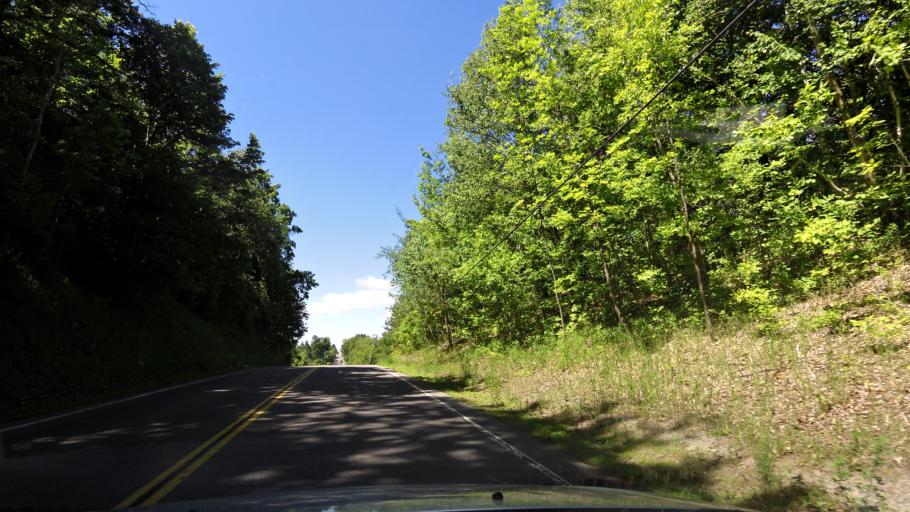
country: CA
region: Ontario
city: Newmarket
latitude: 43.9562
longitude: -79.5357
